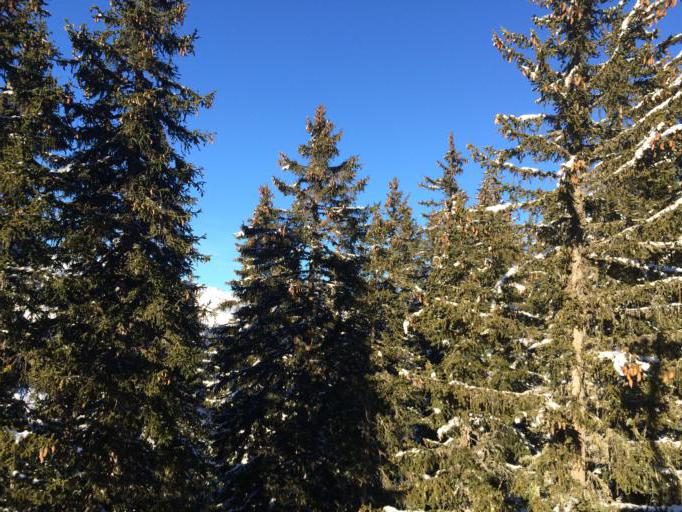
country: CH
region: Grisons
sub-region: Praettigau/Davos District
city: Davos
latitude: 46.7447
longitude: 9.7949
